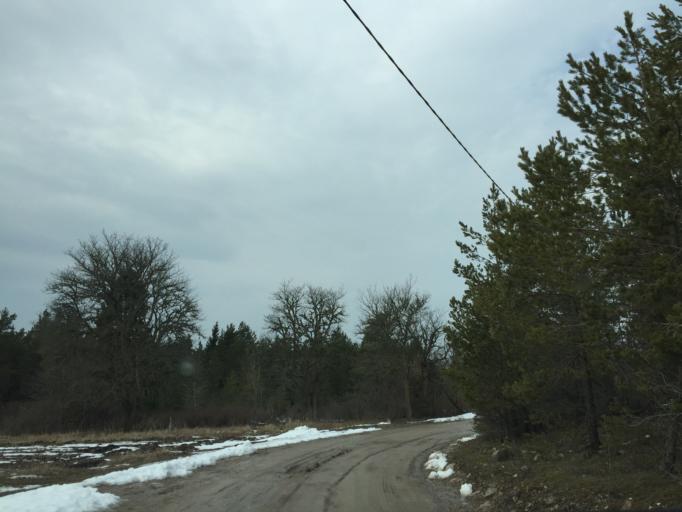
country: EE
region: Saare
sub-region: Kuressaare linn
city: Kuressaare
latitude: 58.4277
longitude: 22.1454
